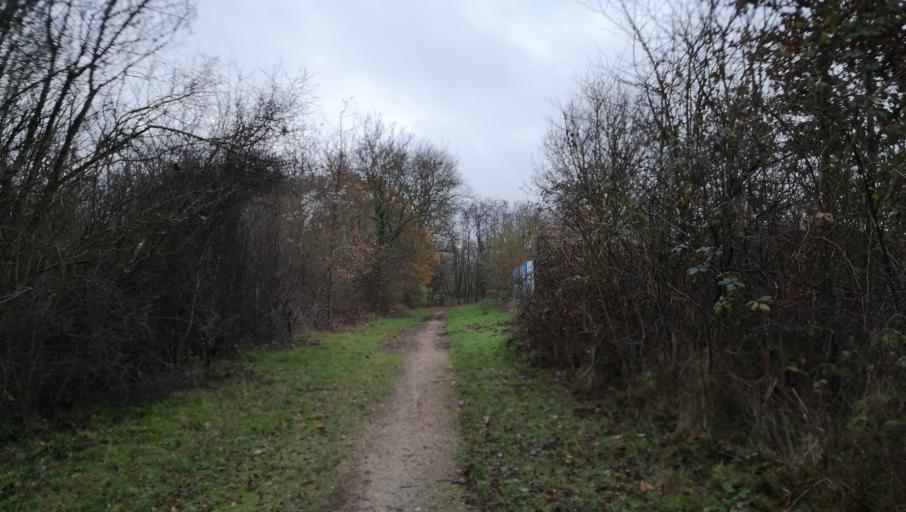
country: FR
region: Centre
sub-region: Departement du Loiret
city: Semoy
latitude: 47.9263
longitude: 1.9562
